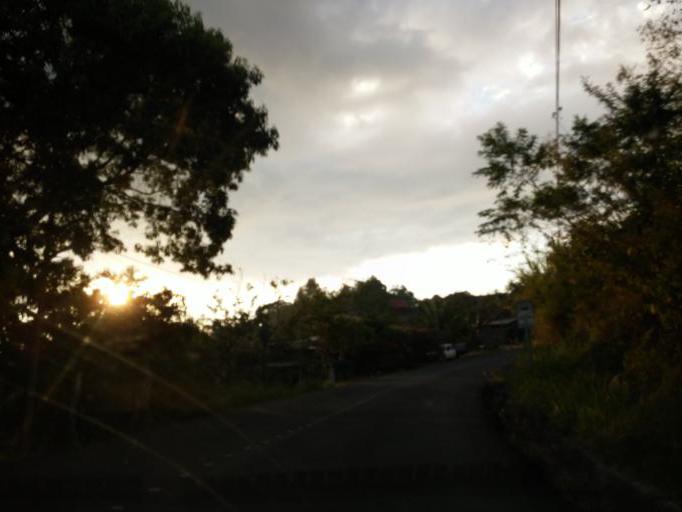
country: CR
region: San Jose
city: Palmichal
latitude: 9.8333
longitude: -84.2076
